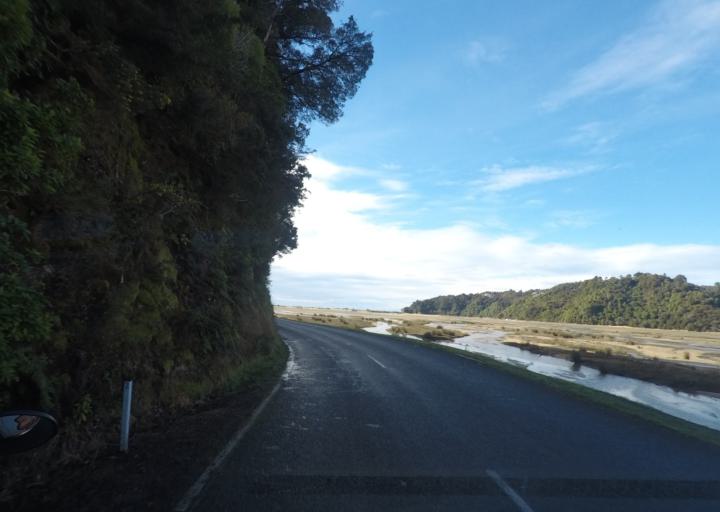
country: NZ
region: Tasman
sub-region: Tasman District
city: Motueka
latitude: -41.0142
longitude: 172.9969
